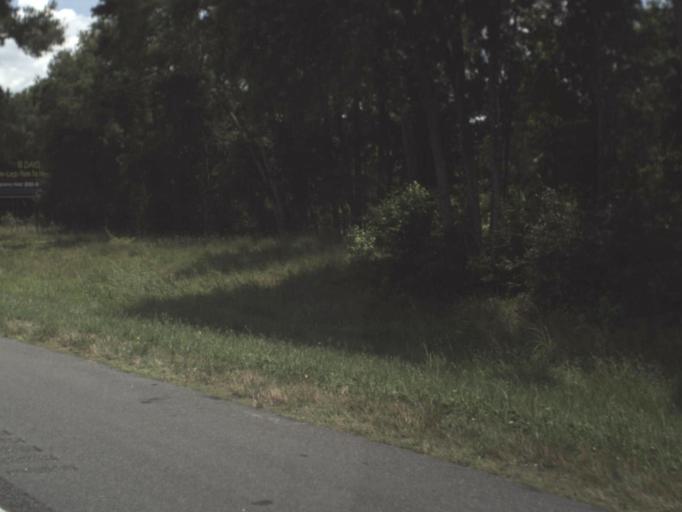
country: US
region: Florida
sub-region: Hamilton County
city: Jasper
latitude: 30.4731
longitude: -82.9733
